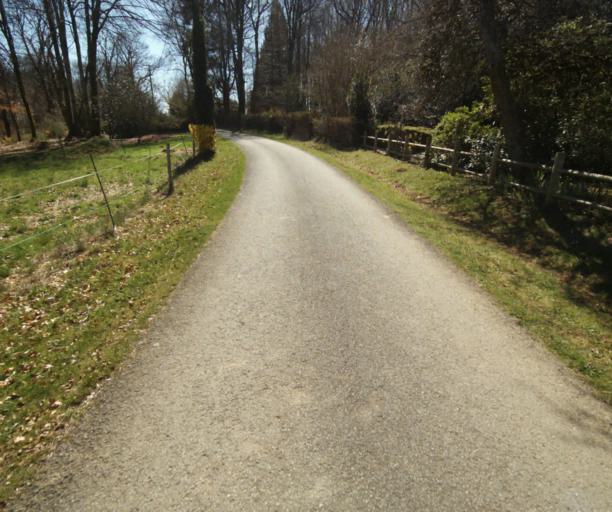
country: FR
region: Limousin
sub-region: Departement de la Correze
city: Uzerche
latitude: 45.3893
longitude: 1.6066
